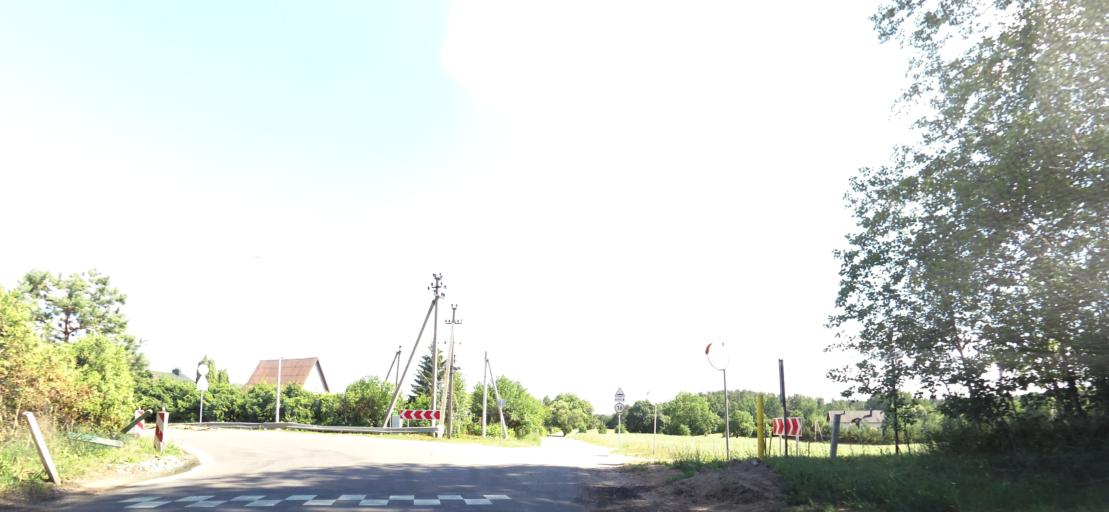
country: LT
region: Vilnius County
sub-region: Vilnius
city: Fabijoniskes
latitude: 54.8001
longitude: 25.3330
